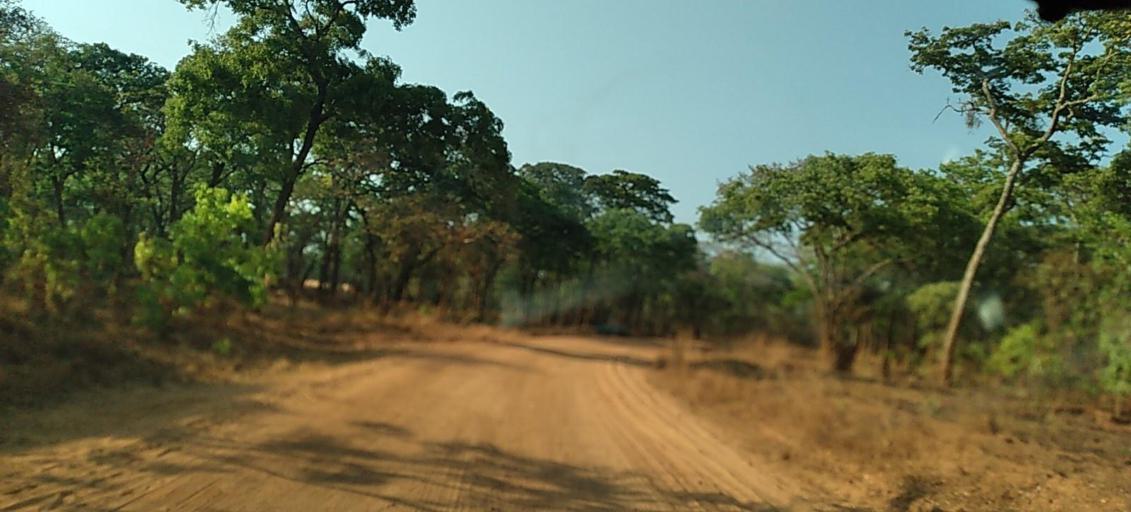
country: ZM
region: North-Western
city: Kasempa
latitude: -13.5583
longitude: 26.0000
